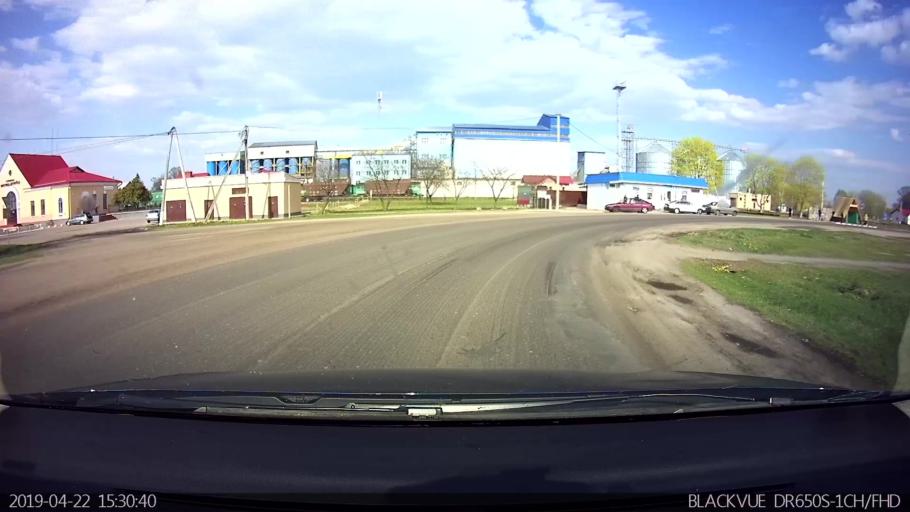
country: BY
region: Brest
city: Vysokaye
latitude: 52.3996
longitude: 23.3809
